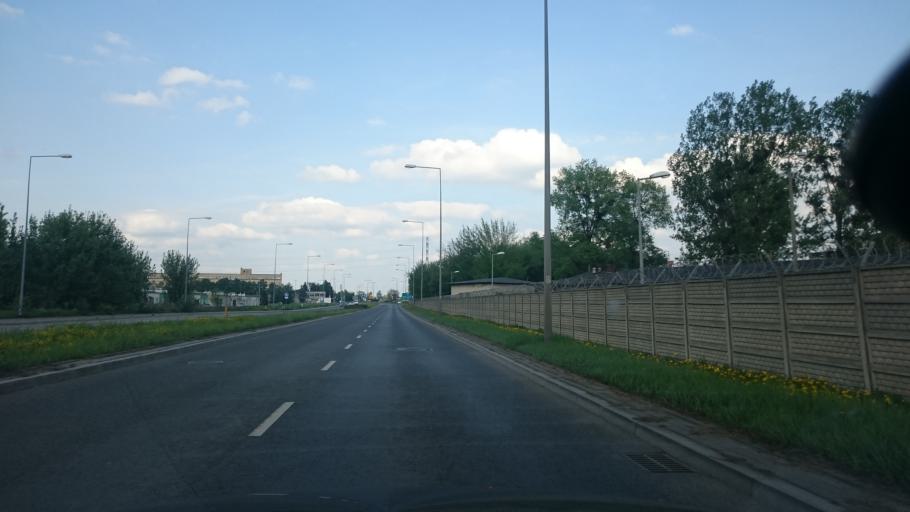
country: PL
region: Kujawsko-Pomorskie
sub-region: Grudziadz
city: Grudziadz
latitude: 53.4748
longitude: 18.7752
